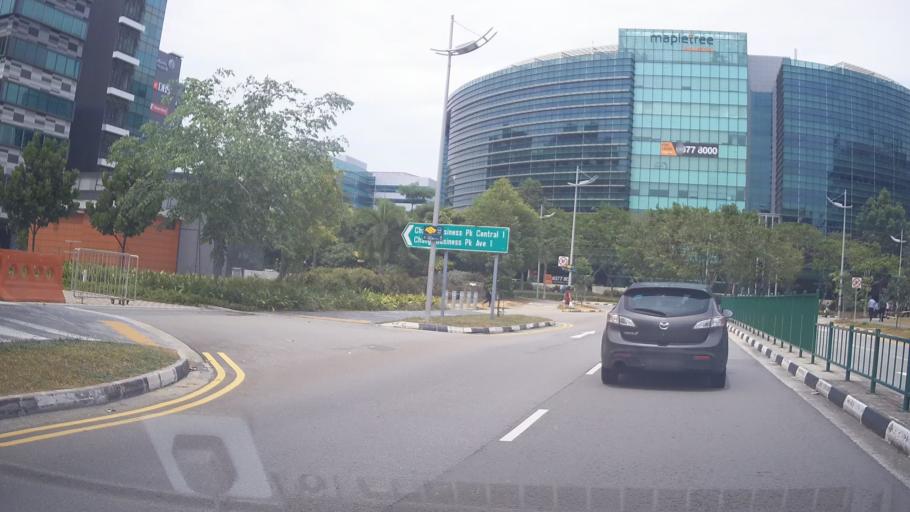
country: SG
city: Singapore
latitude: 1.3337
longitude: 103.9643
